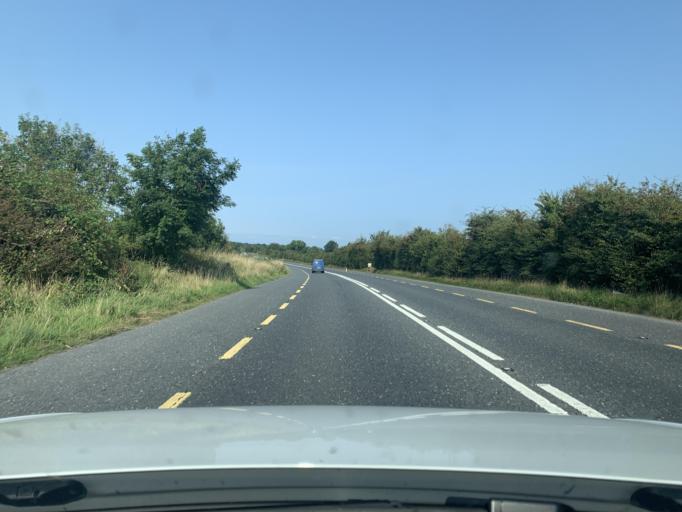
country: IE
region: Leinster
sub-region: An Iarmhi
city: Athlone
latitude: 53.5324
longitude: -8.0542
